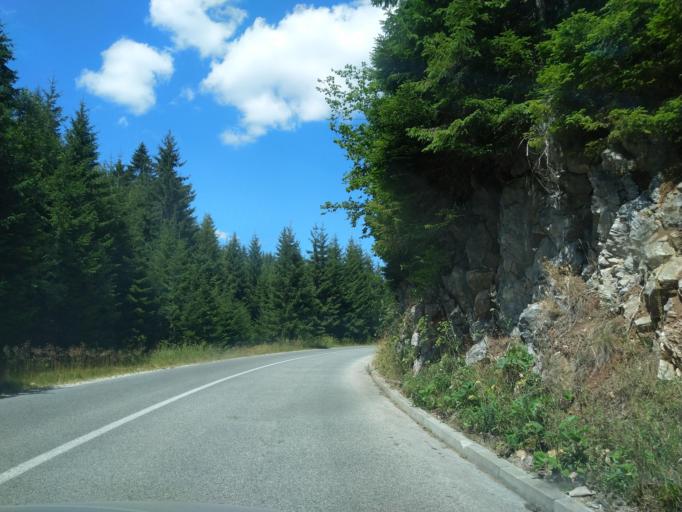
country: RS
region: Central Serbia
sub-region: Zlatiborski Okrug
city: Nova Varos
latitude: 43.3973
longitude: 19.8435
